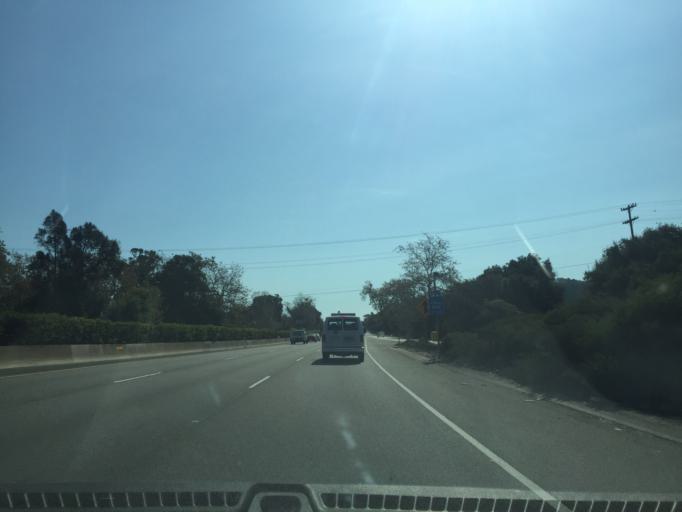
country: US
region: California
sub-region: Santa Barbara County
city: Santa Barbara
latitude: 34.4250
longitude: -119.7198
